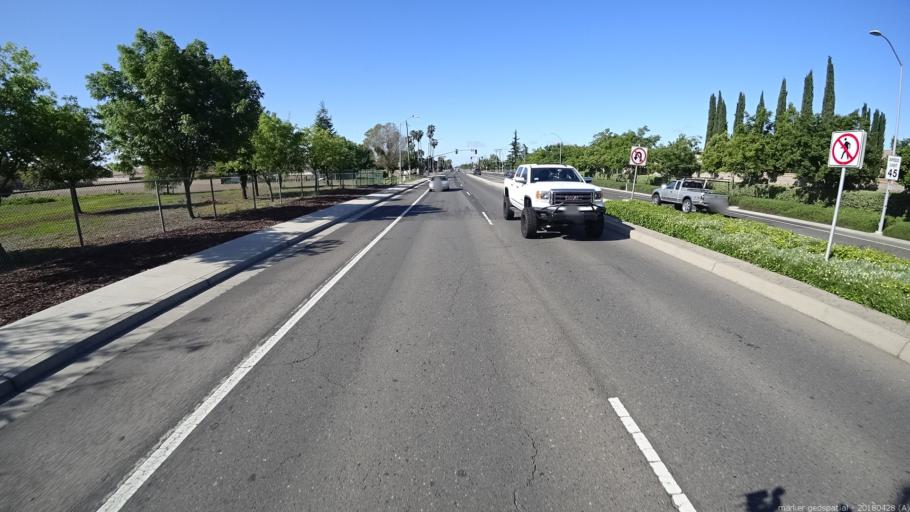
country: US
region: California
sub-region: Yolo County
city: West Sacramento
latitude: 38.5476
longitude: -121.5419
